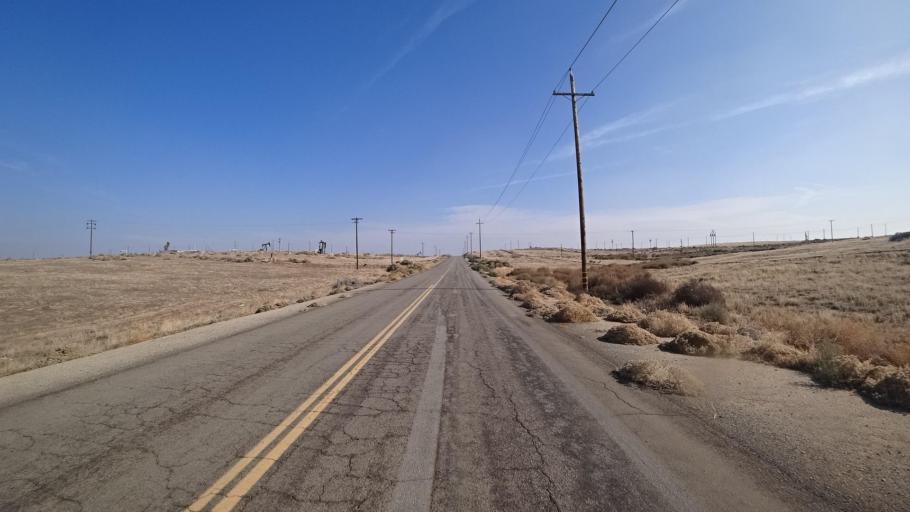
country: US
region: California
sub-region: Kern County
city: Oildale
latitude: 35.5303
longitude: -119.0943
